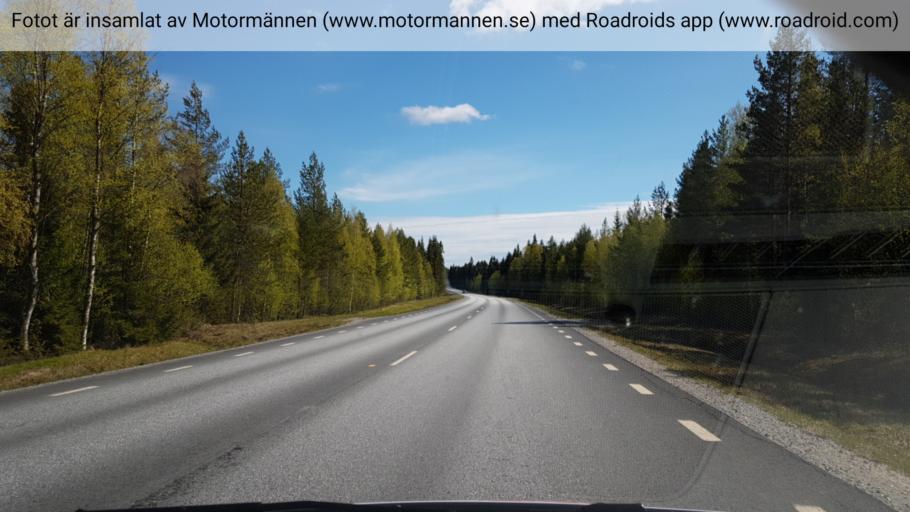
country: SE
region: Vaesterbotten
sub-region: Vannas Kommun
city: Vannasby
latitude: 64.0842
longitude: 19.9781
